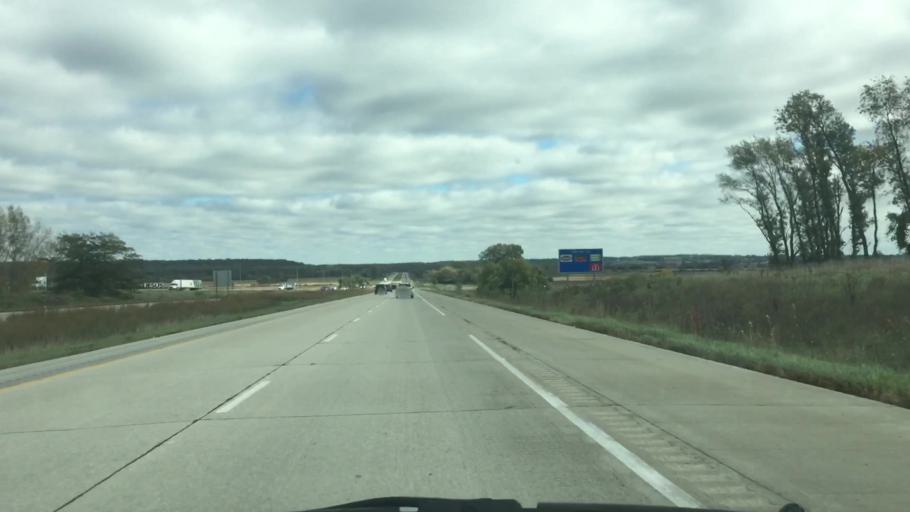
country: US
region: Iowa
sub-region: Polk County
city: Mitchellville
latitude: 41.6819
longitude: -93.3325
